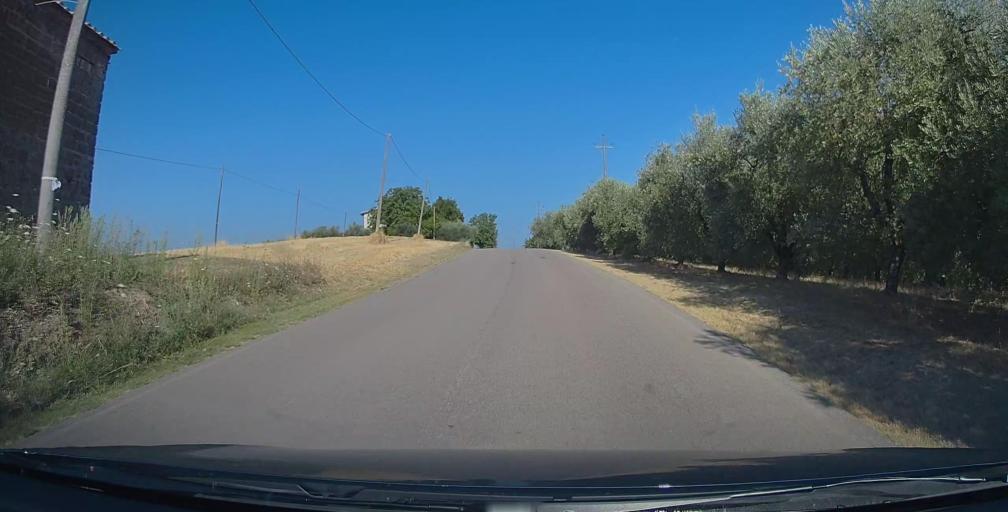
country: IT
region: Umbria
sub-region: Provincia di Terni
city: Otricoli
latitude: 42.4067
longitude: 12.5056
